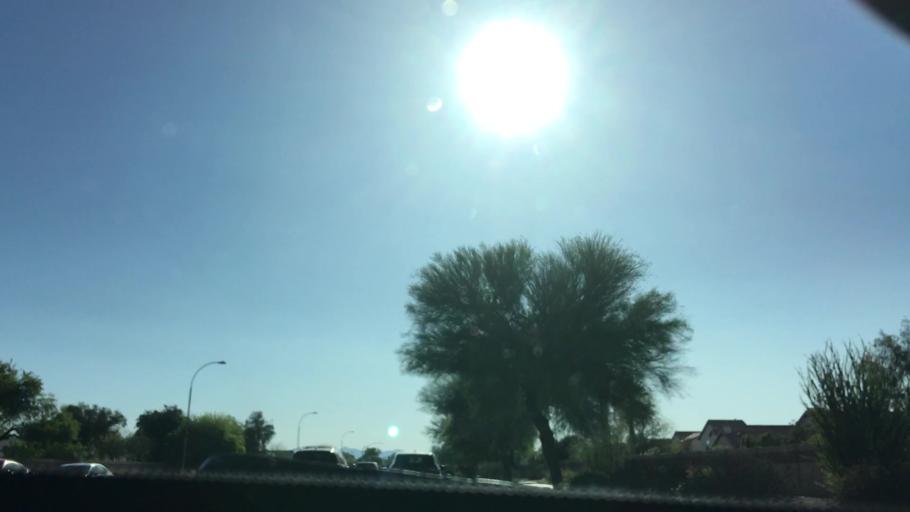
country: US
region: Arizona
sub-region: Maricopa County
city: Peoria
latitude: 33.6107
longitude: -112.2259
